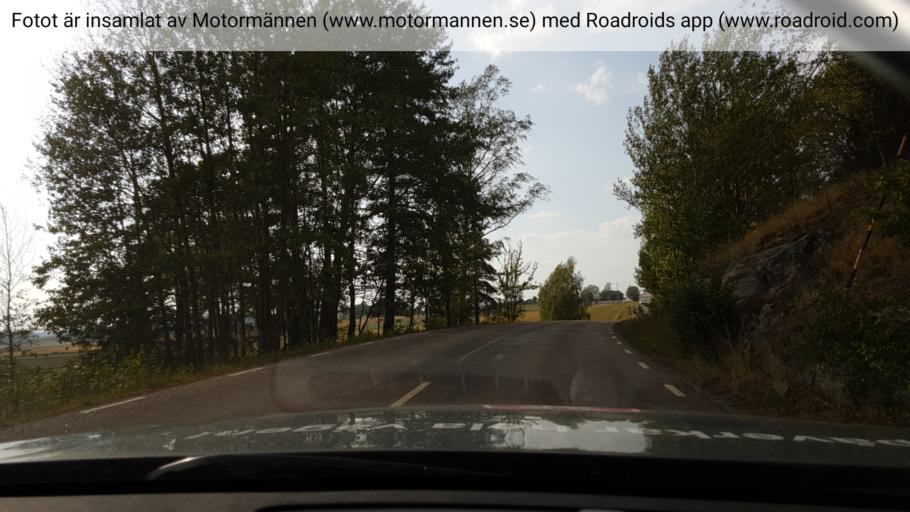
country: SE
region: Soedermanland
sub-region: Gnesta Kommun
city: Gnesta
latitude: 59.0984
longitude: 17.2343
